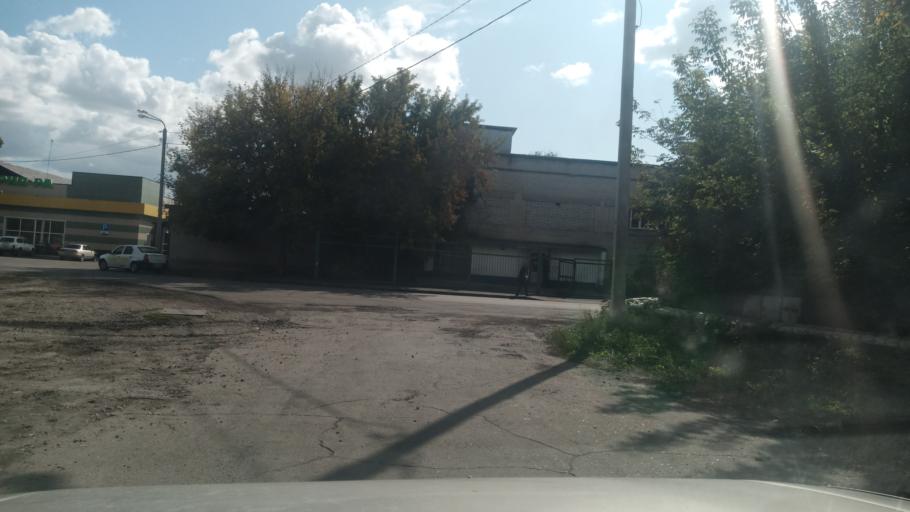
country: RU
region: Altai Krai
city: Zaton
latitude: 53.2977
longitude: 83.8013
